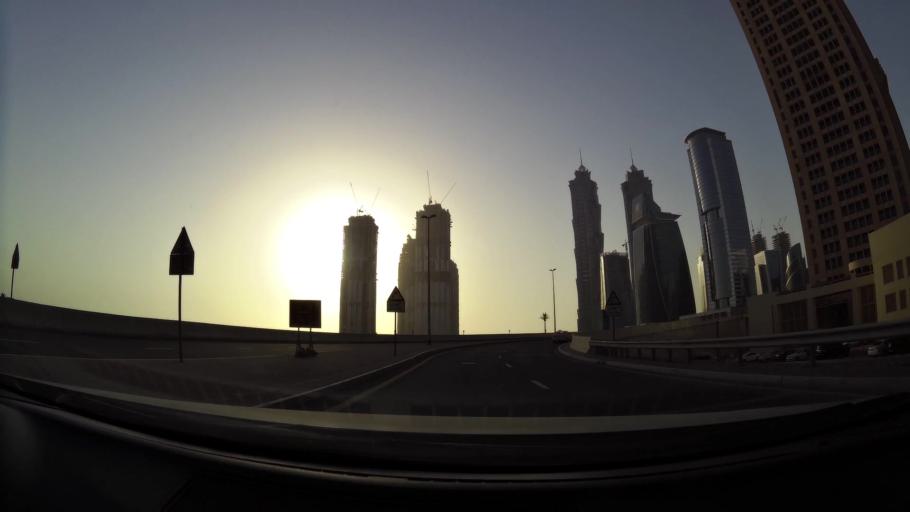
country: AE
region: Dubai
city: Dubai
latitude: 25.1801
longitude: 55.2622
